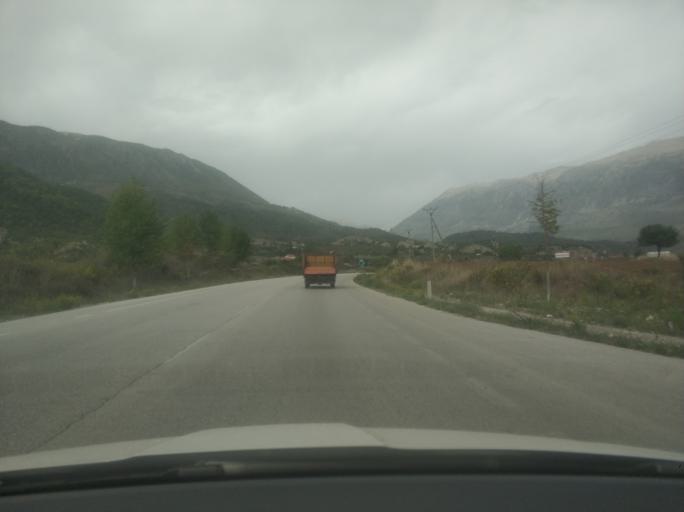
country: AL
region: Gjirokaster
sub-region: Rrethi i Gjirokastres
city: Picar
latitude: 40.1819
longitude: 20.0764
